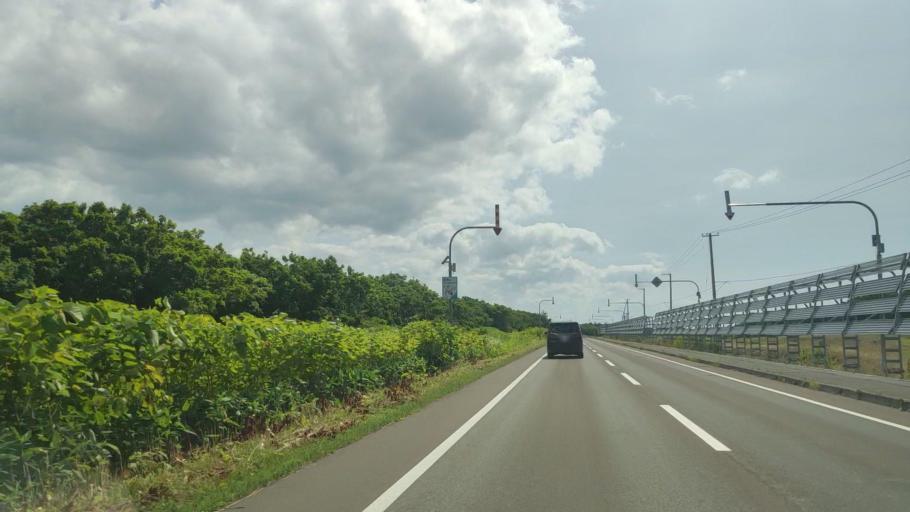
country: JP
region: Hokkaido
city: Makubetsu
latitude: 44.9117
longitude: 141.7386
